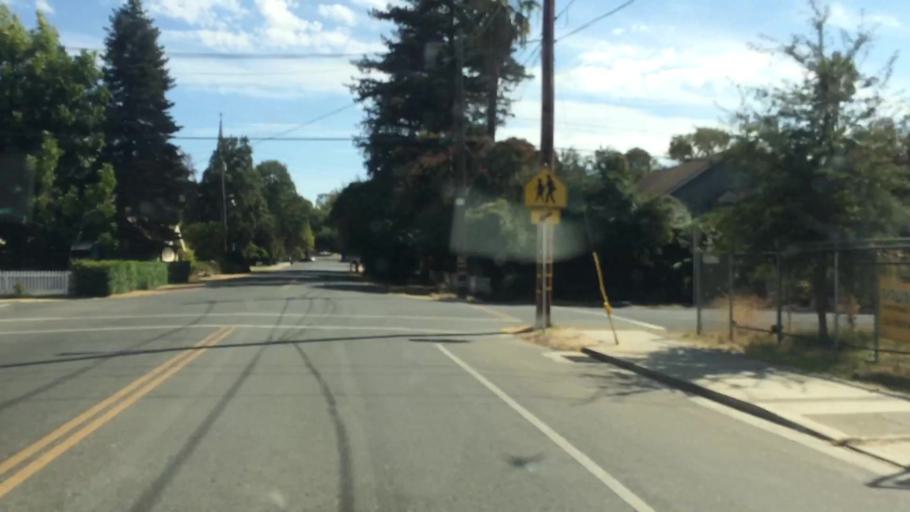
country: US
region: California
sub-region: Amador County
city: Ione
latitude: 38.3519
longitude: -120.9350
